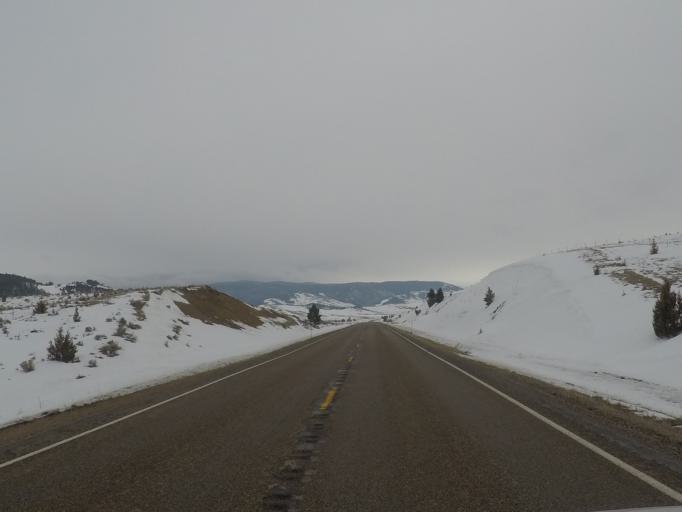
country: US
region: Montana
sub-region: Meagher County
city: White Sulphur Springs
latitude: 46.6220
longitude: -110.8467
